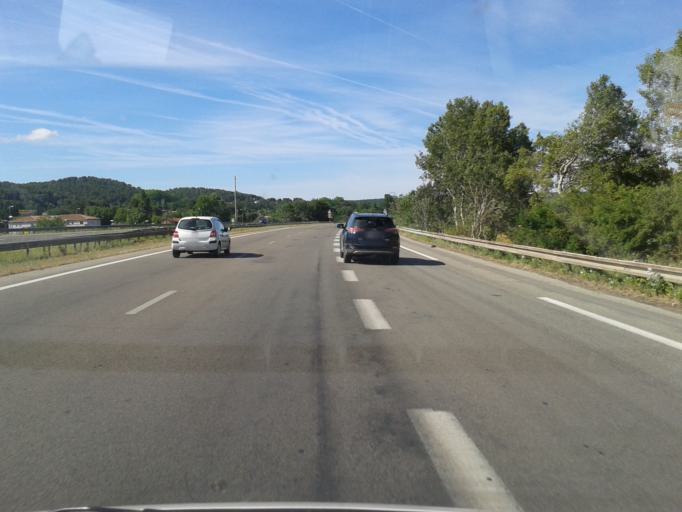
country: FR
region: Provence-Alpes-Cote d'Azur
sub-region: Departement des Bouches-du-Rhone
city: Bouc-Bel-Air
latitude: 43.4635
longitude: 5.4064
